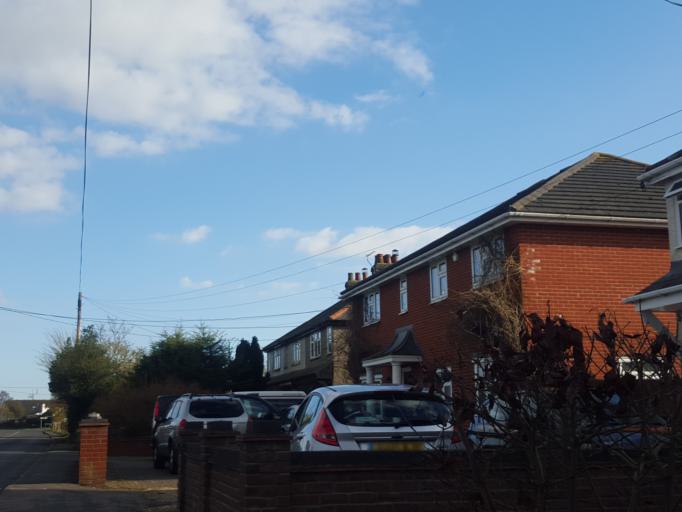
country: GB
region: England
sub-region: Essex
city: Little Clacton
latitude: 51.8455
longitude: 1.1220
